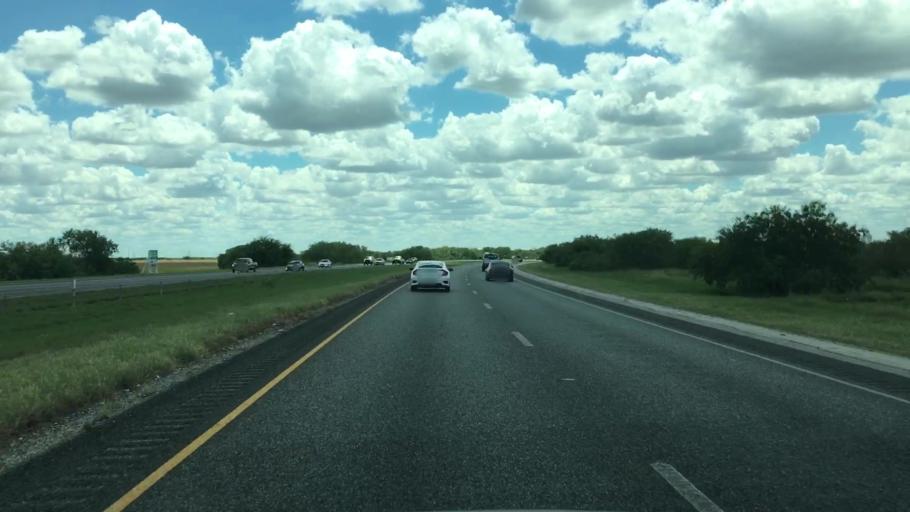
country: US
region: Texas
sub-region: Bexar County
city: Elmendorf
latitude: 29.3013
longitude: -98.3958
